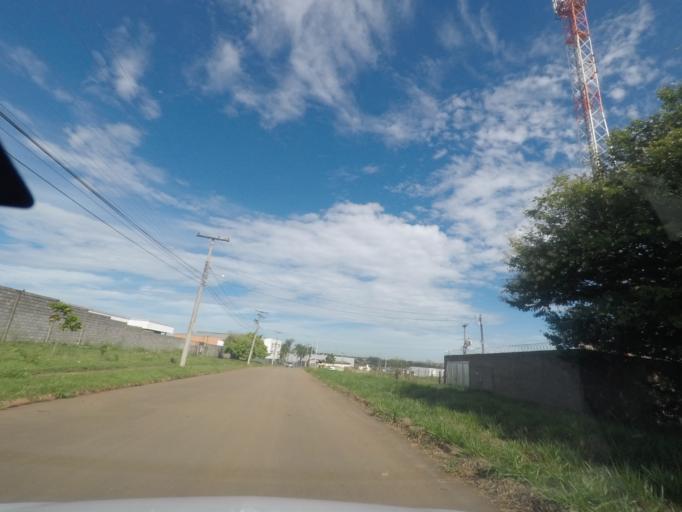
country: BR
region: Goias
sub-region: Aparecida De Goiania
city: Aparecida de Goiania
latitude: -16.7909
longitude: -49.2536
